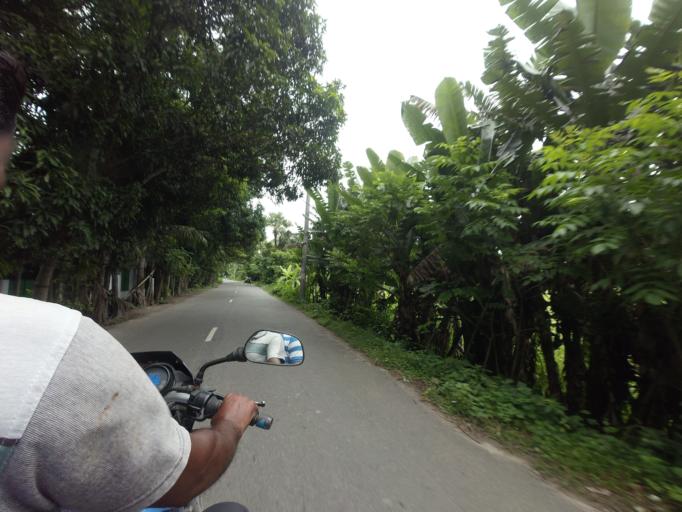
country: BD
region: Khulna
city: Kalia
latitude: 23.1693
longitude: 89.6455
